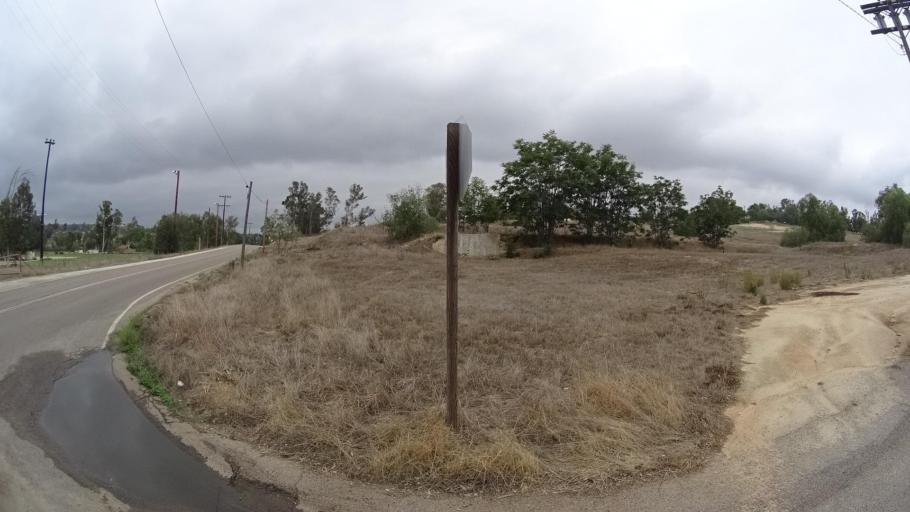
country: US
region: California
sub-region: San Diego County
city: Ramona
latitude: 33.0585
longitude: -116.8608
